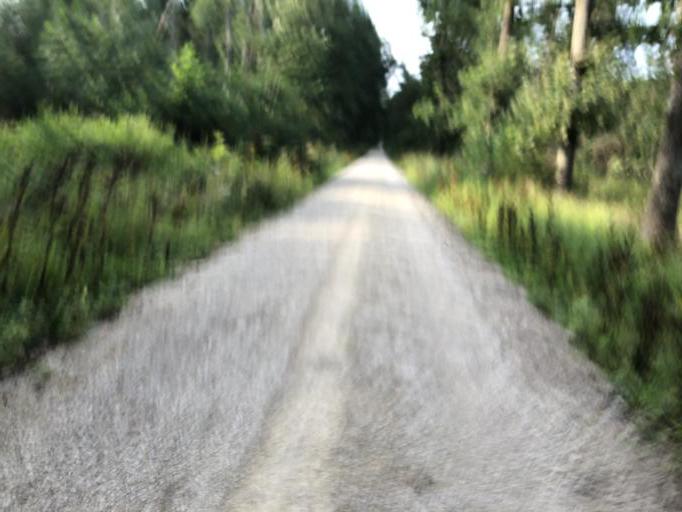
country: DE
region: Bavaria
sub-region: Regierungsbezirk Mittelfranken
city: Uttenreuth
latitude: 49.5743
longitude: 11.0764
